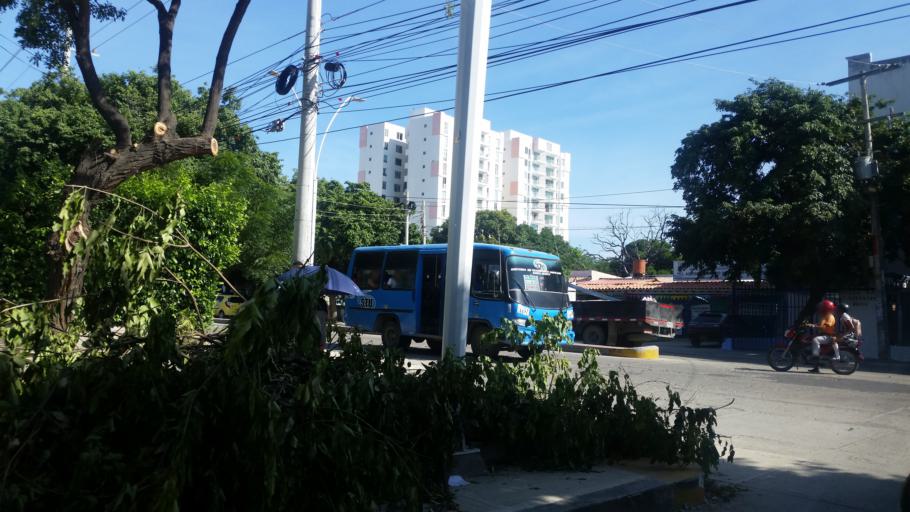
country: CO
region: Magdalena
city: Santa Marta
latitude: 11.2315
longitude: -74.1761
